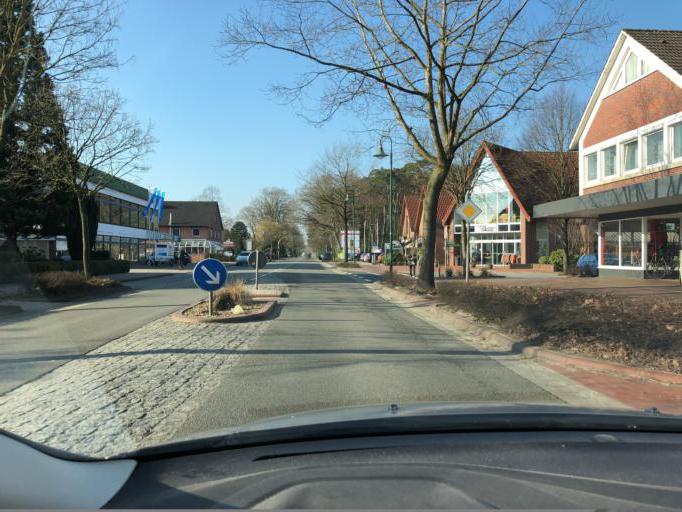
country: DE
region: Lower Saxony
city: Schwerinsdorf
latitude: 53.3046
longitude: 7.7452
